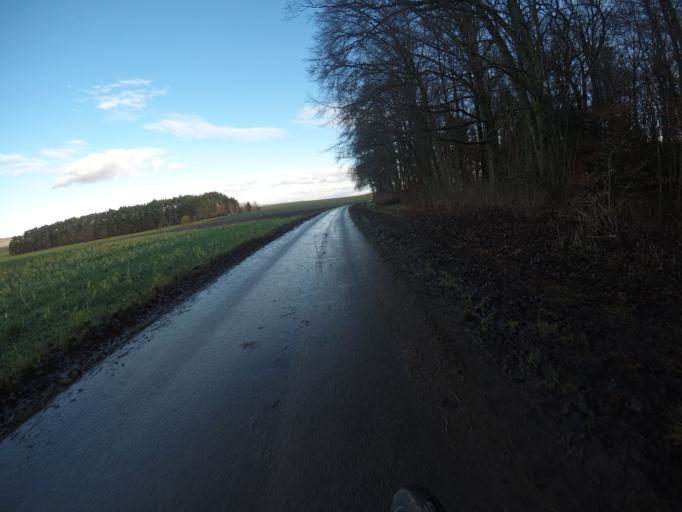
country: DE
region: Baden-Wuerttemberg
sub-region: Regierungsbezirk Stuttgart
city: Bondorf
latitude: 48.5269
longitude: 8.8940
